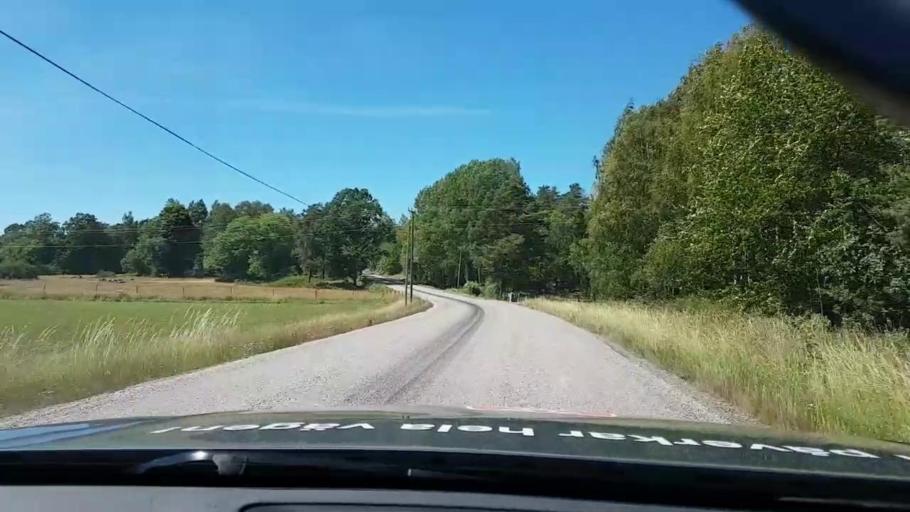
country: SE
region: Kalmar
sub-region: Vasterviks Kommun
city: Vaestervik
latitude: 57.9096
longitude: 16.6516
